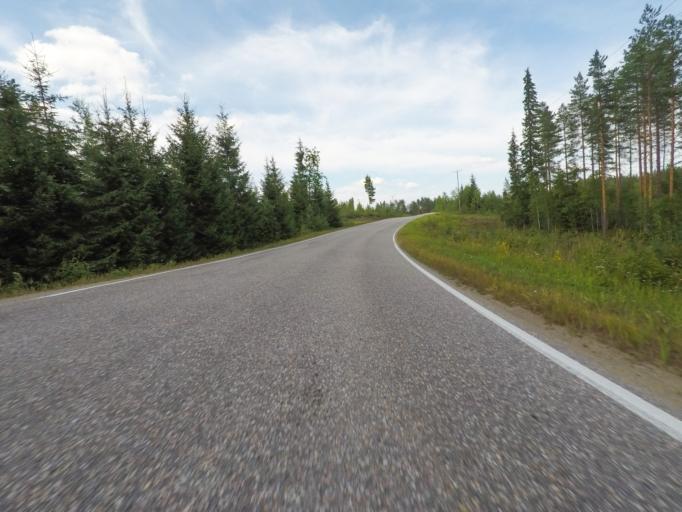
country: FI
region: Southern Savonia
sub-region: Savonlinna
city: Sulkava
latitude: 61.7413
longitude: 28.1978
